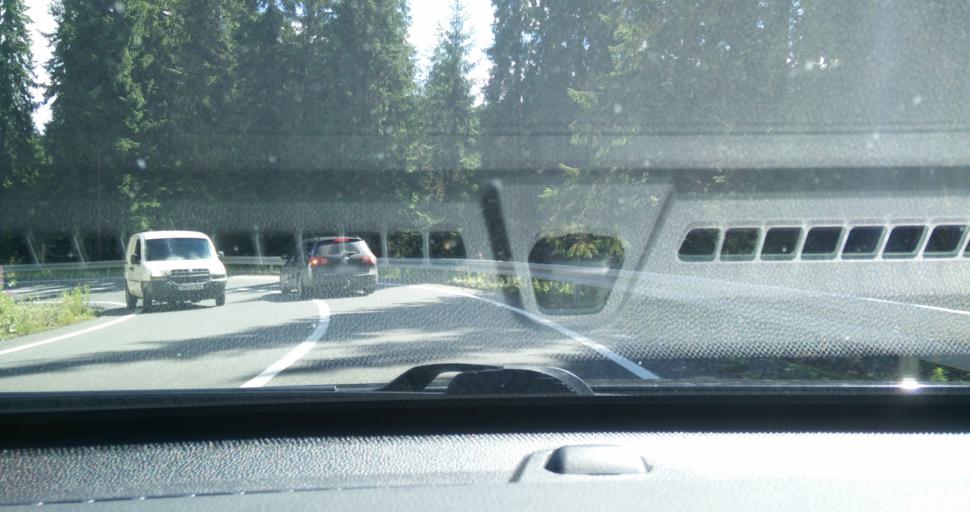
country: RO
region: Hunedoara
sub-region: Oras Petrila
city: Petrila
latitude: 45.5040
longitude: 23.6486
